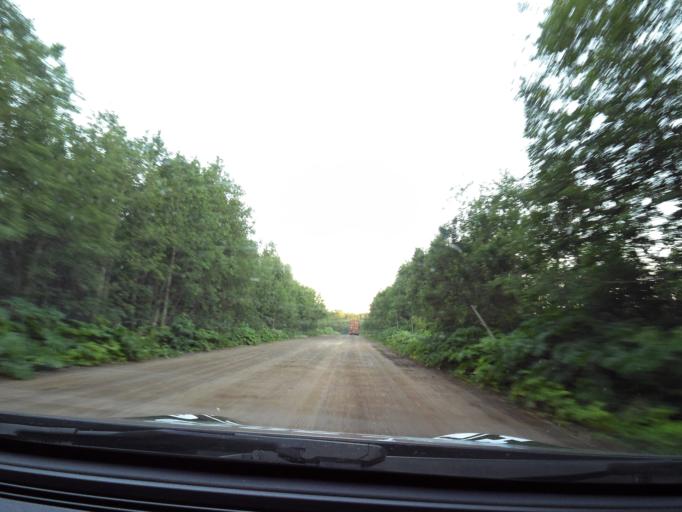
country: RU
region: Leningrad
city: Voznesen'ye
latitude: 60.9332
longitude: 35.4712
